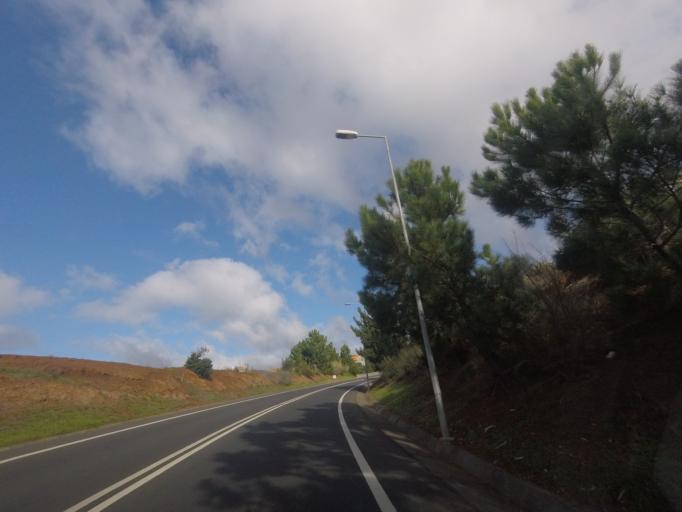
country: PT
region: Madeira
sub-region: Calheta
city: Estreito da Calheta
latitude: 32.7509
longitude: -17.2134
